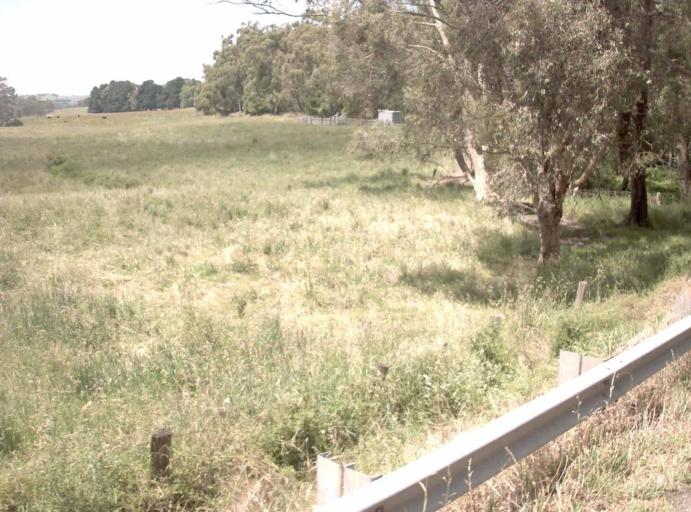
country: AU
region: Victoria
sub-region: Bass Coast
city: North Wonthaggi
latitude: -38.6021
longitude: 146.0189
